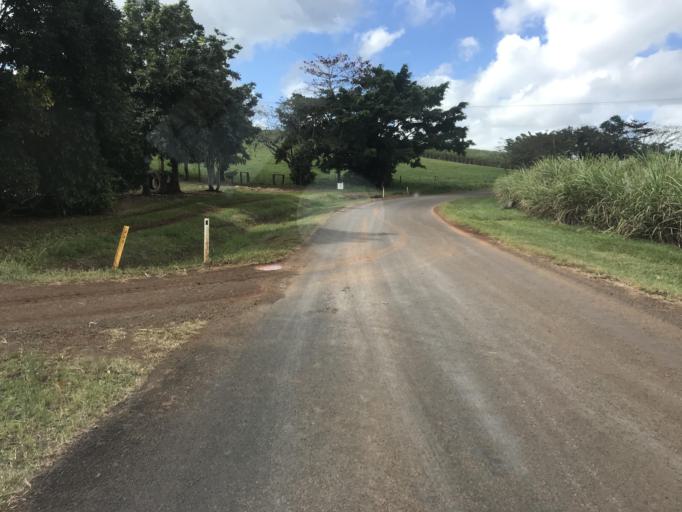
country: AU
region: Queensland
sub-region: Cassowary Coast
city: Innisfail
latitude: -17.5492
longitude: 145.8700
